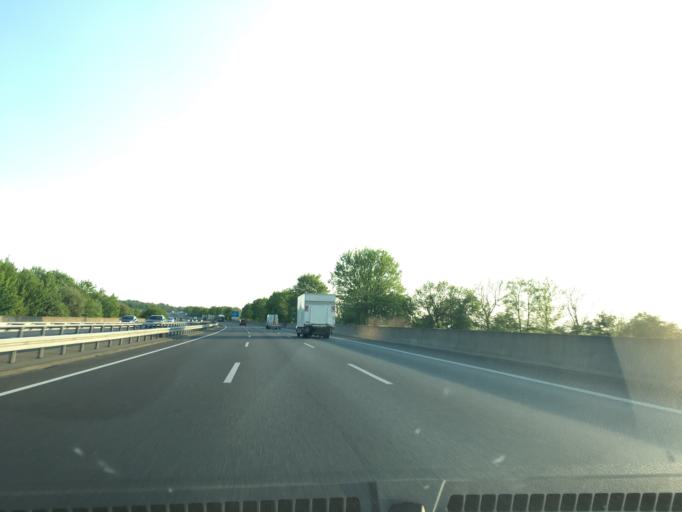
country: DE
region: Lower Saxony
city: Pohle
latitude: 52.2495
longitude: 9.2921
